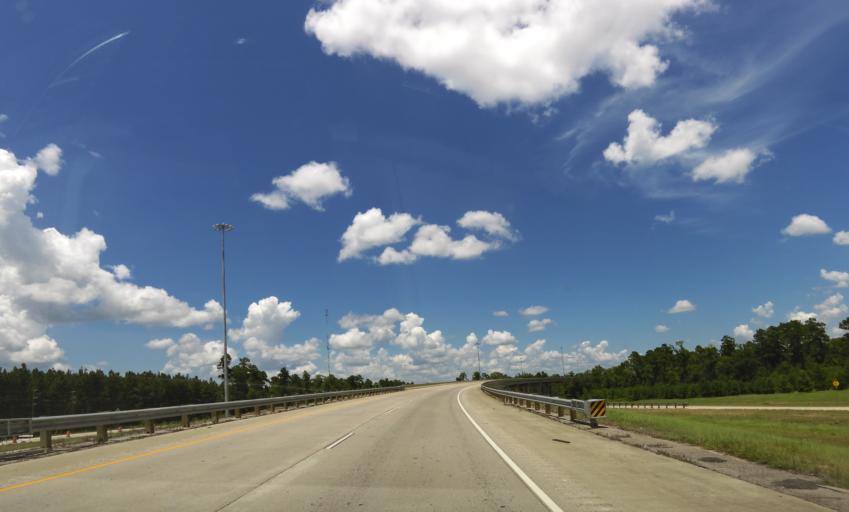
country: US
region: Texas
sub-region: San Jacinto County
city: Shepherd
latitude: 30.4697
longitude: -95.0165
